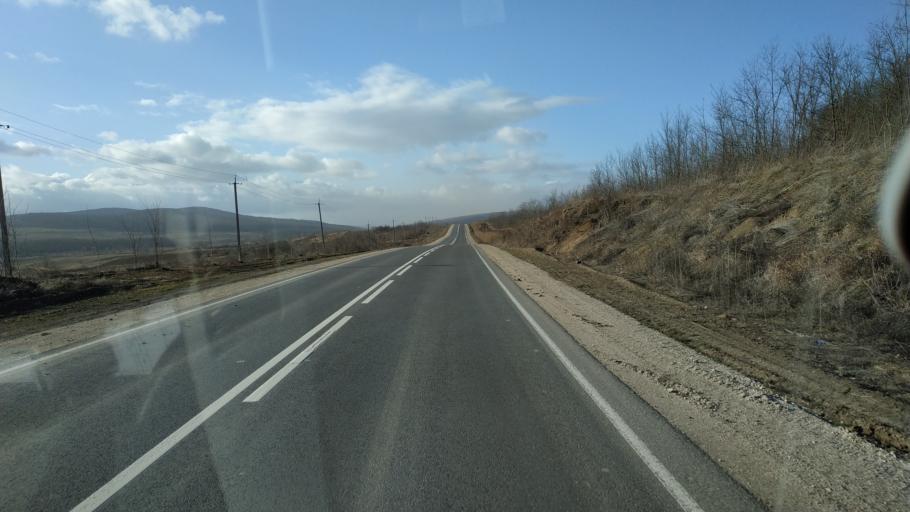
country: MD
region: Calarasi
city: Calarasi
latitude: 47.3078
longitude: 28.1291
